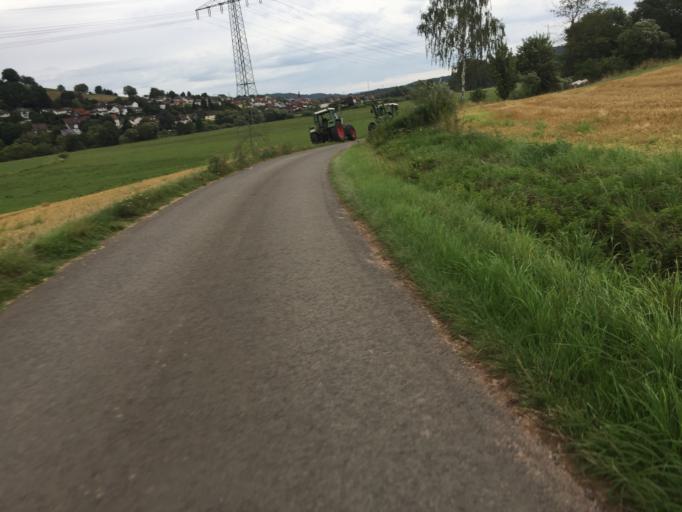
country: DE
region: Hesse
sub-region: Regierungsbezirk Kassel
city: Bad Hersfeld
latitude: 50.8892
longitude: 9.7363
